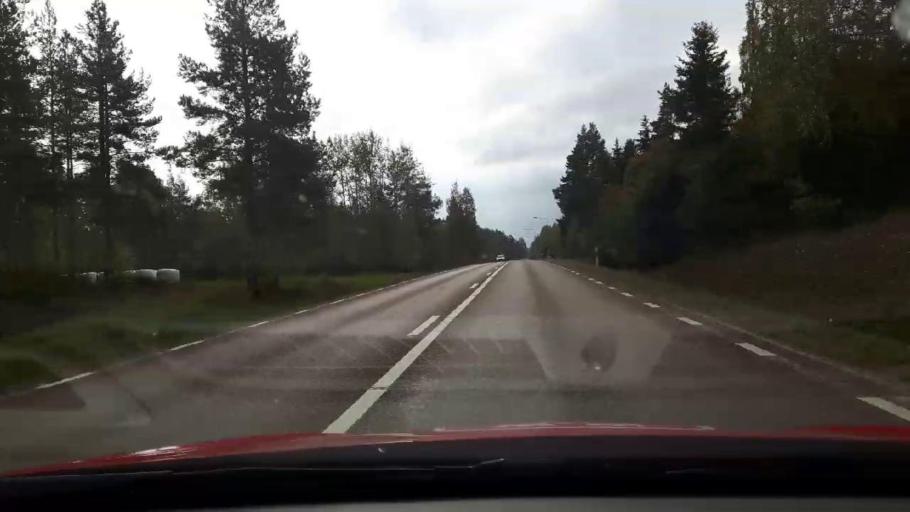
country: SE
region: Gaevleborg
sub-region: Bollnas Kommun
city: Kilafors
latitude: 61.2548
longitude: 16.5521
